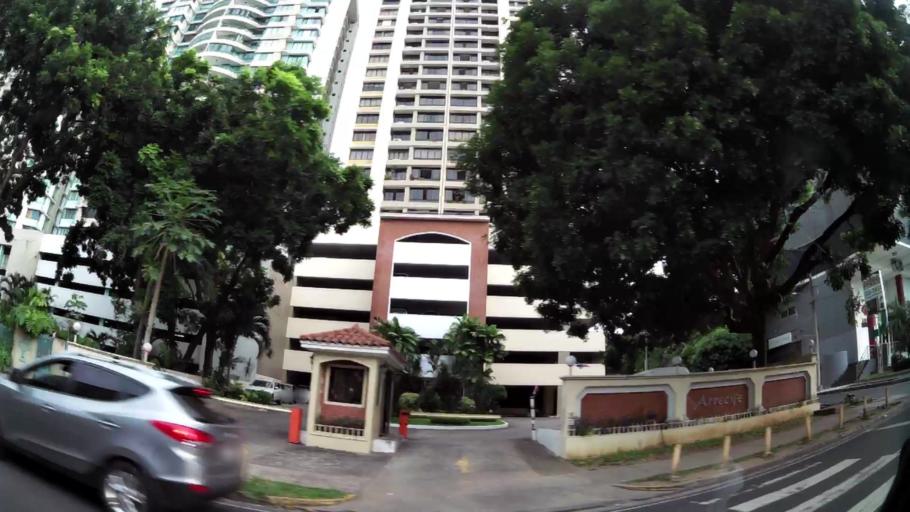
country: PA
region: Panama
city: Panama
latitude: 8.9781
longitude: -79.5148
